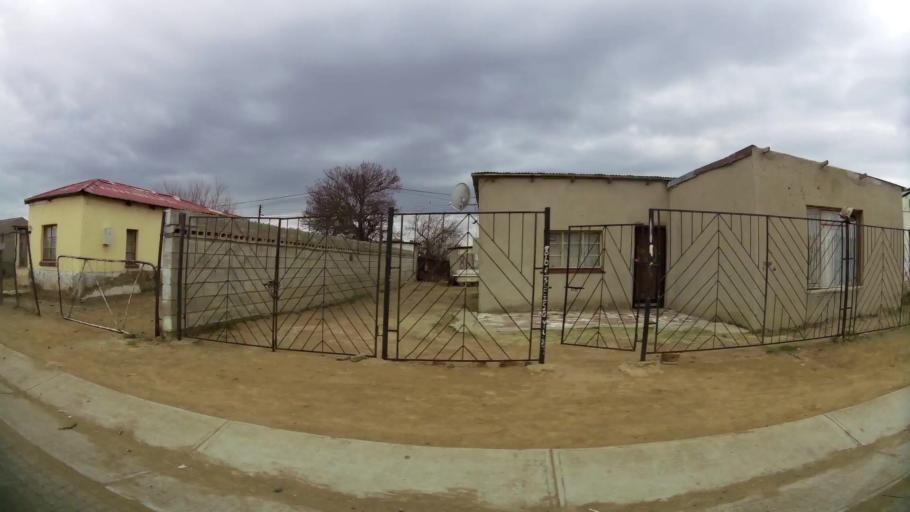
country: ZA
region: Orange Free State
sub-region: Fezile Dabi District Municipality
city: Kroonstad
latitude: -27.6480
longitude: 27.2046
